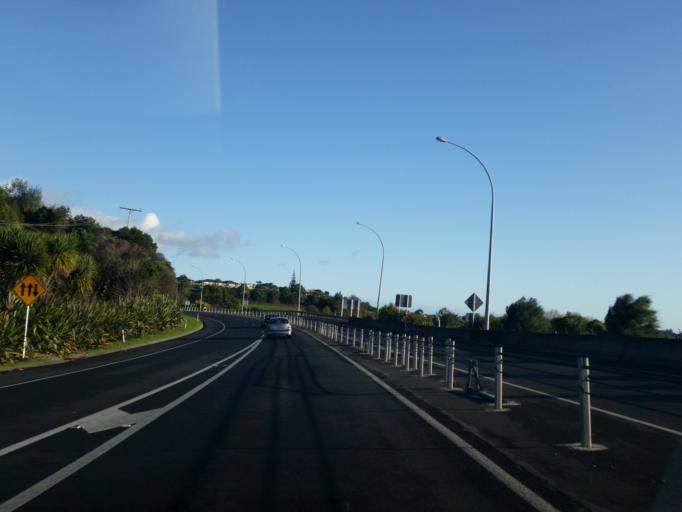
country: NZ
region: Bay of Plenty
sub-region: Tauranga City
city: Tauranga
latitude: -37.6952
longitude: 176.1258
